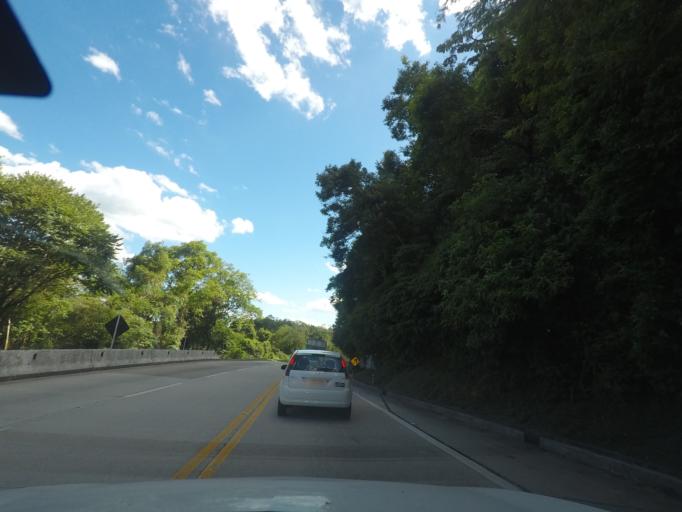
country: BR
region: Rio de Janeiro
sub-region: Guapimirim
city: Guapimirim
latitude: -22.4794
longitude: -42.9960
